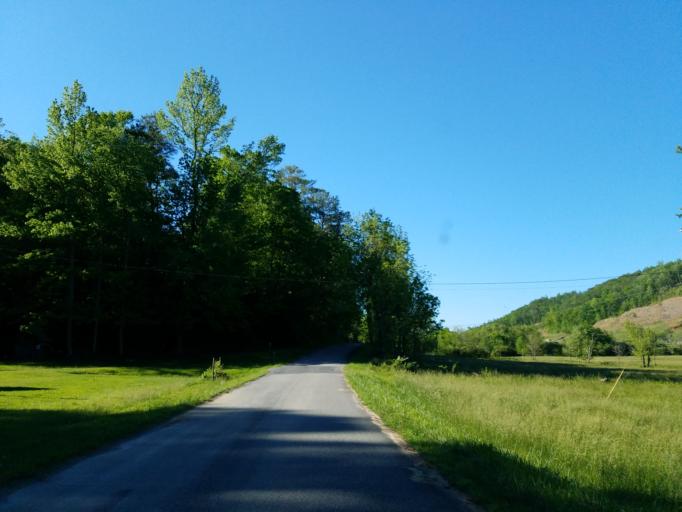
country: US
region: Georgia
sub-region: Gilmer County
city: Ellijay
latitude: 34.5887
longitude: -84.5110
